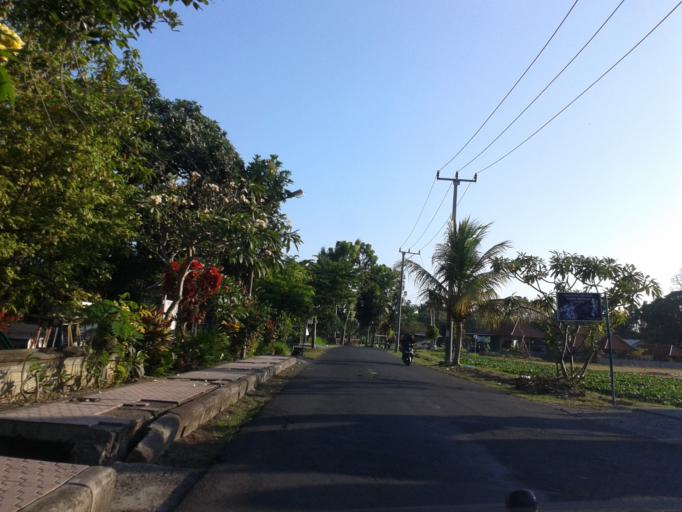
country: ID
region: Bali
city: Klungkung
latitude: -8.5566
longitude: 115.3875
